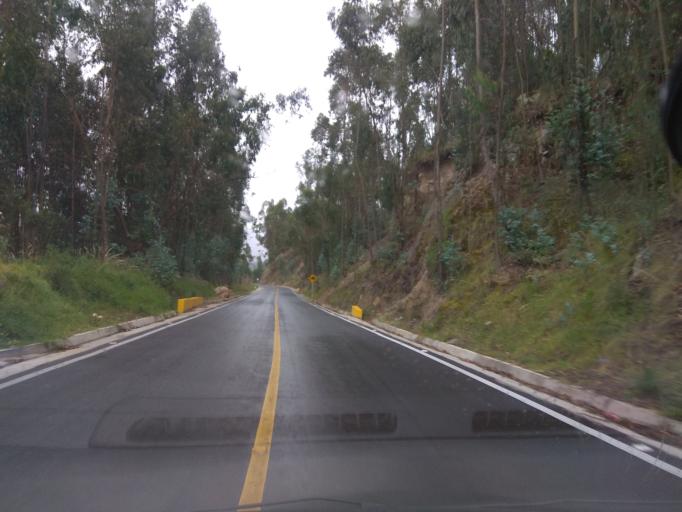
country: CO
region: Boyaca
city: Mongui
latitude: 5.7355
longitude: -72.8505
